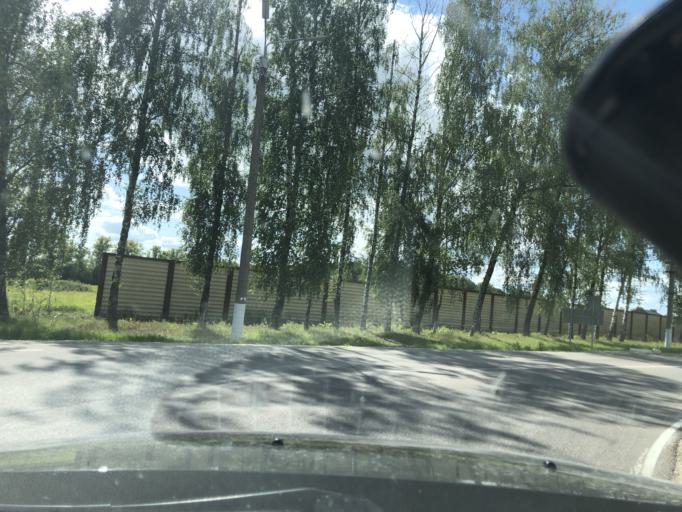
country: RU
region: Tula
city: Gorelki
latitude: 54.3365
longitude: 37.5630
